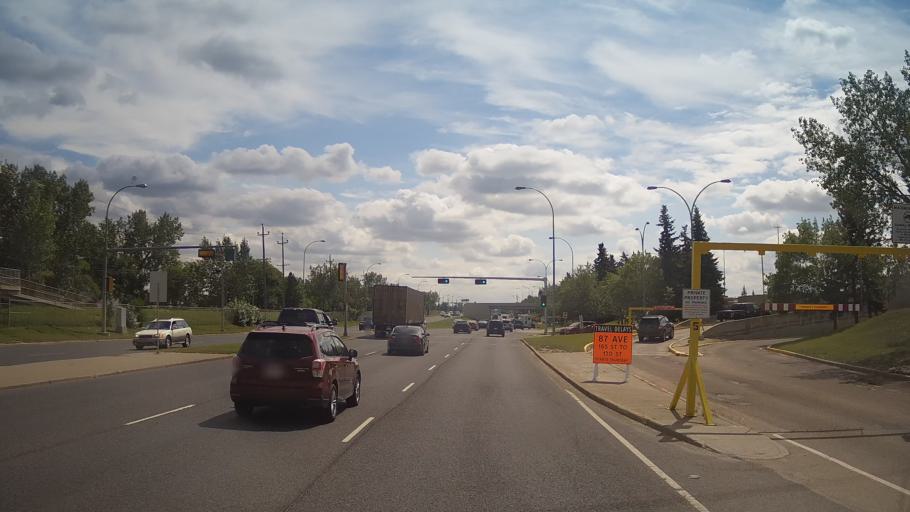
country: CA
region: Alberta
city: St. Albert
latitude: 53.5238
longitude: -113.6155
